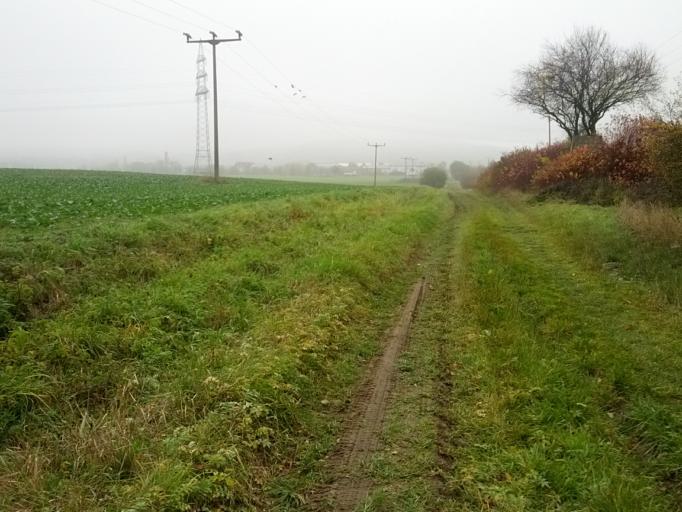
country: DE
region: Thuringia
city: Bischofroda
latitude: 51.0003
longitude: 10.3727
